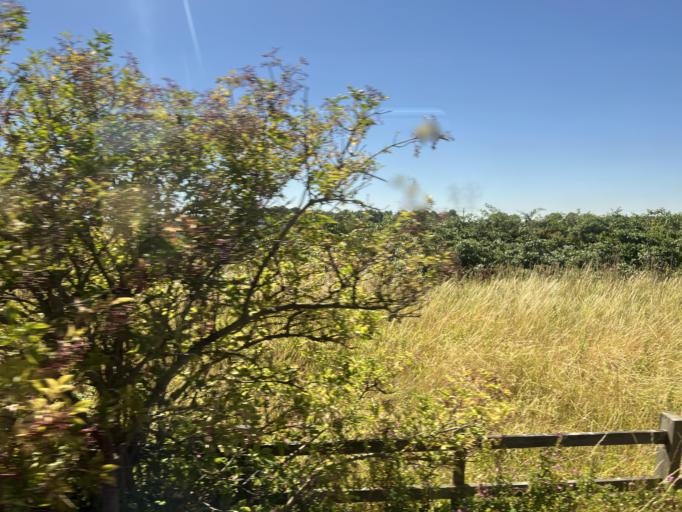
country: GB
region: England
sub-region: Lincolnshire
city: Wainfleet All Saints
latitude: 53.1073
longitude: 0.2299
